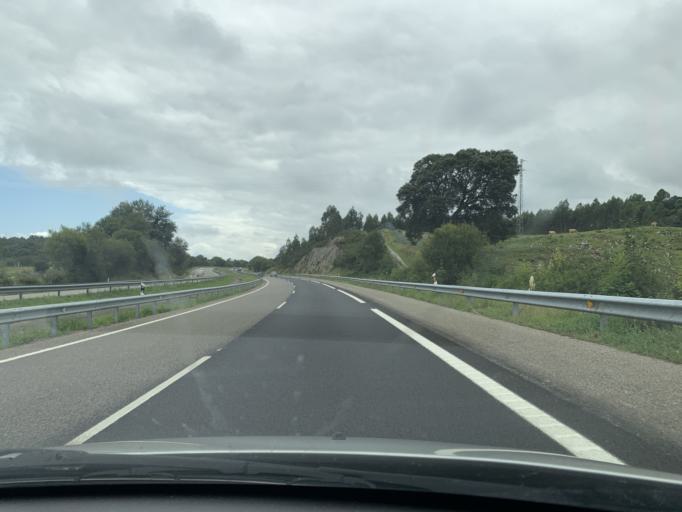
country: ES
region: Asturias
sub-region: Province of Asturias
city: Llanes
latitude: 43.4230
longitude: -4.8051
